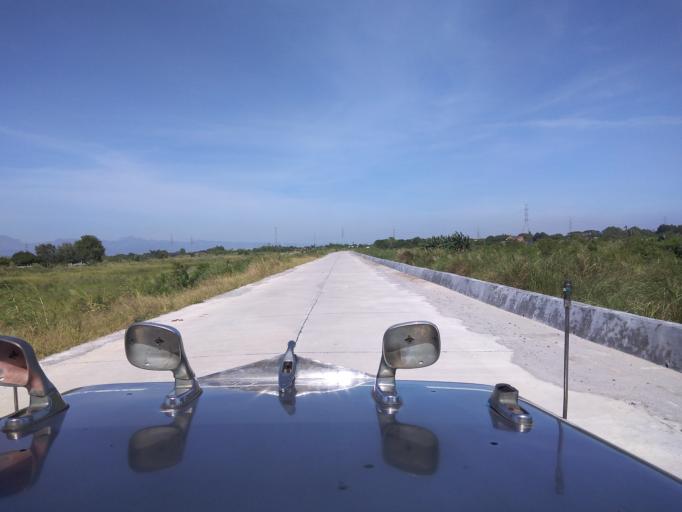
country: PH
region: Central Luzon
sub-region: Province of Pampanga
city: Bacolor
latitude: 14.9995
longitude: 120.6630
